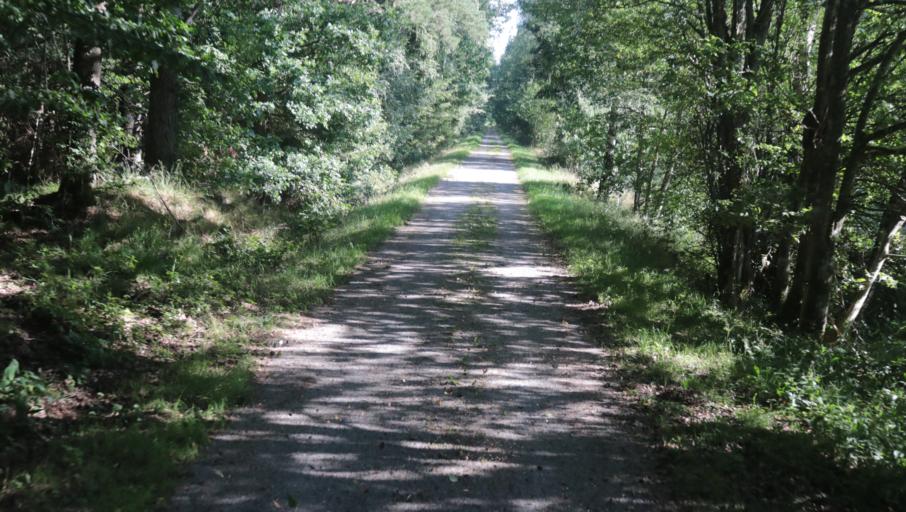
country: SE
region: Blekinge
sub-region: Karlshamns Kommun
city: Svangsta
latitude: 56.3424
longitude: 14.6963
